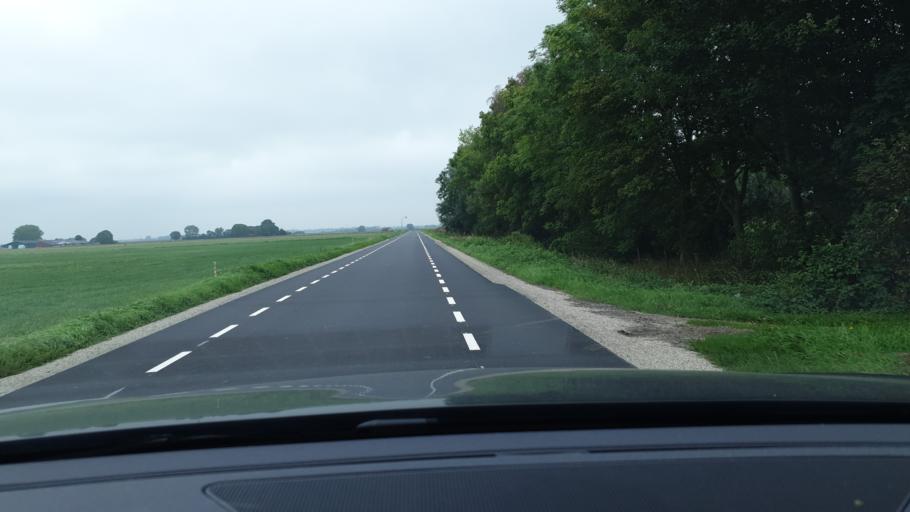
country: NL
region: North Brabant
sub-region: Gemeente Maasdonk
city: Geffen
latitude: 51.7737
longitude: 5.4312
